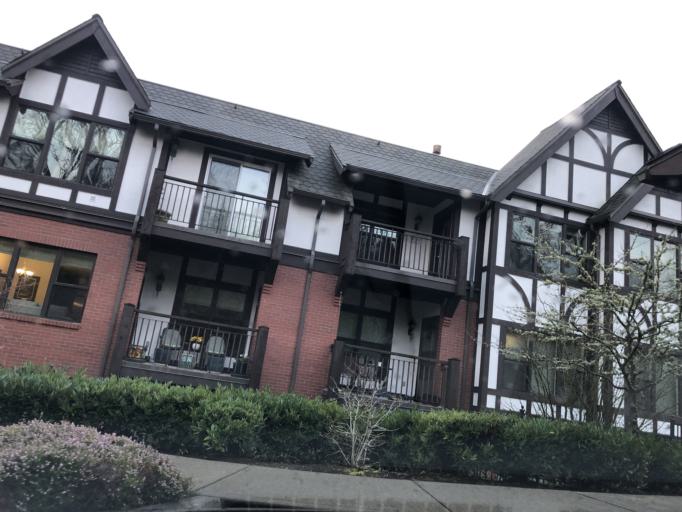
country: US
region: Washington
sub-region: Pierce County
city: Fircrest
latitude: 47.3016
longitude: -122.5208
